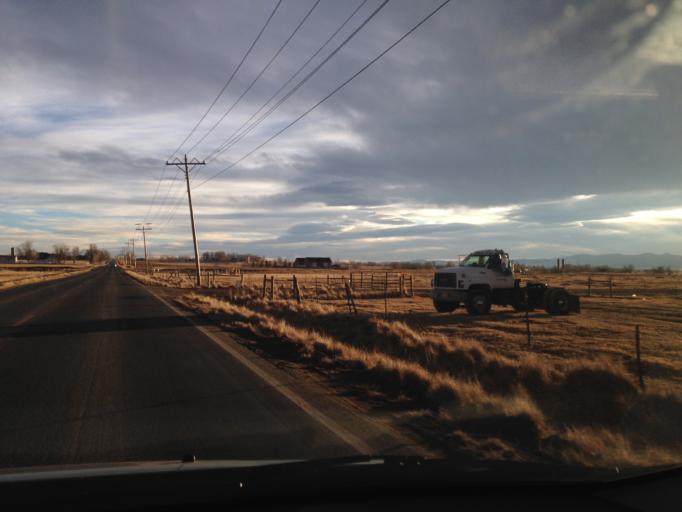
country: US
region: Colorado
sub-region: Weld County
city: Firestone
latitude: 40.1293
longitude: -104.9989
